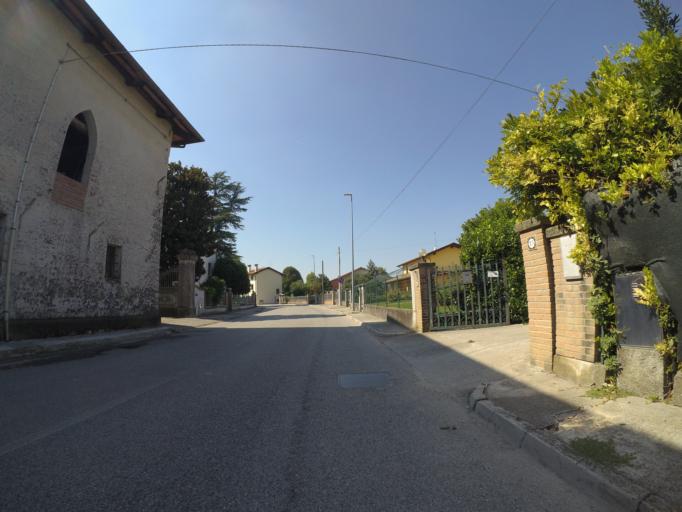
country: IT
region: Friuli Venezia Giulia
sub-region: Provincia di Udine
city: Camino al Tagliamento
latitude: 45.9155
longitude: 12.9539
